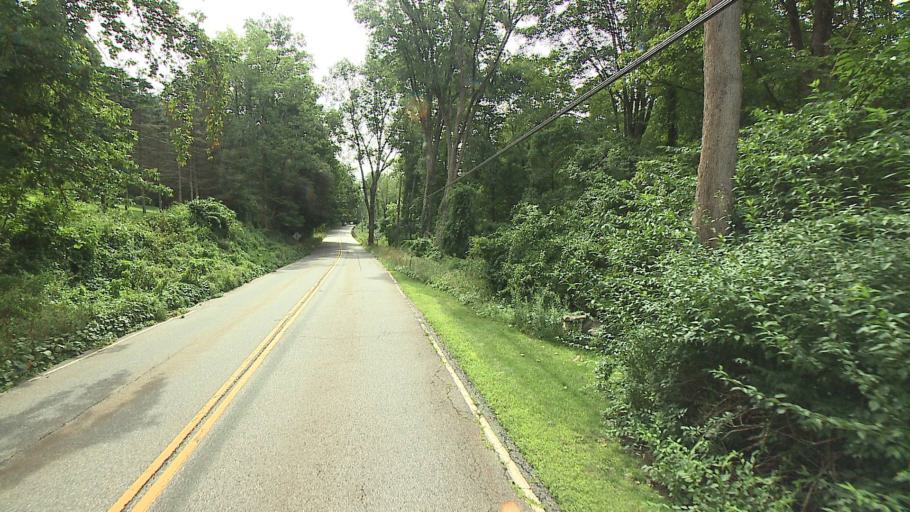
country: US
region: Connecticut
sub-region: Litchfield County
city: Kent
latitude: 41.7460
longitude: -73.5050
